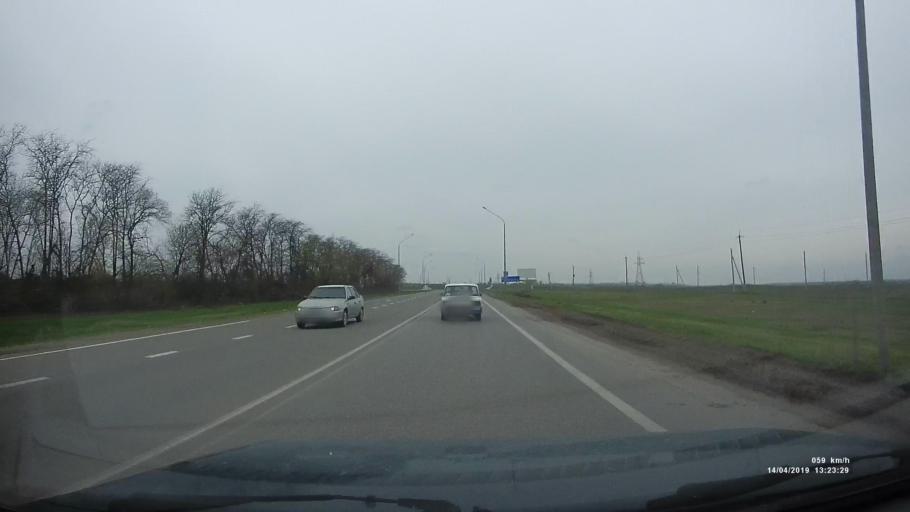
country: RU
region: Rostov
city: Kuleshovka
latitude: 47.0836
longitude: 39.4996
